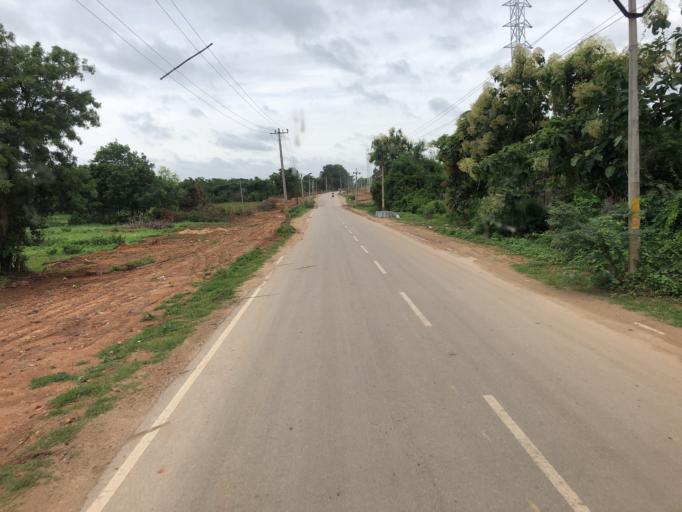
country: IN
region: Telangana
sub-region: Medak
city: Serilingampalle
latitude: 17.4330
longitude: 78.2987
